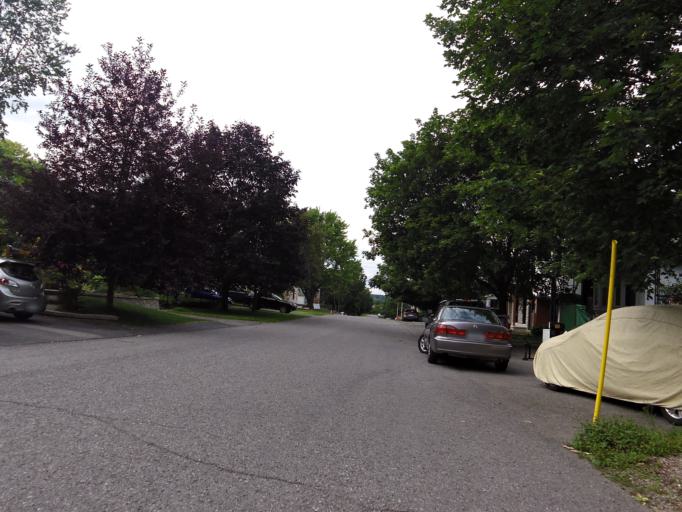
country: CA
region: Ontario
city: Ottawa
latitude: 45.3957
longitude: -75.7584
